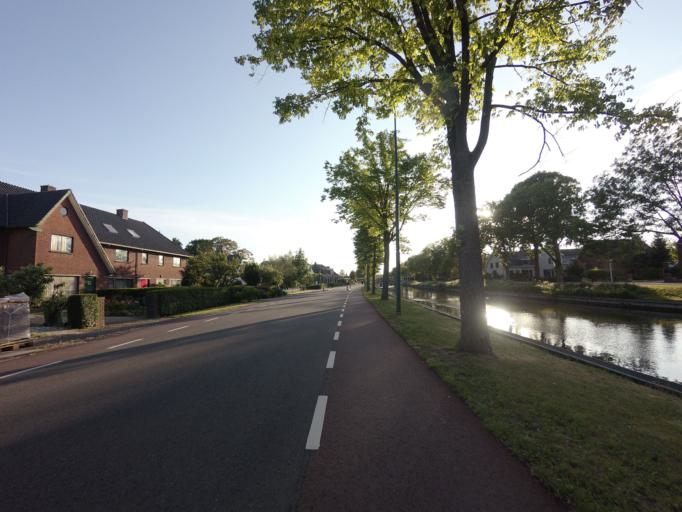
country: NL
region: Utrecht
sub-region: Stichtse Vecht
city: Maarssen
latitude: 52.0819
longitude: 5.0519
